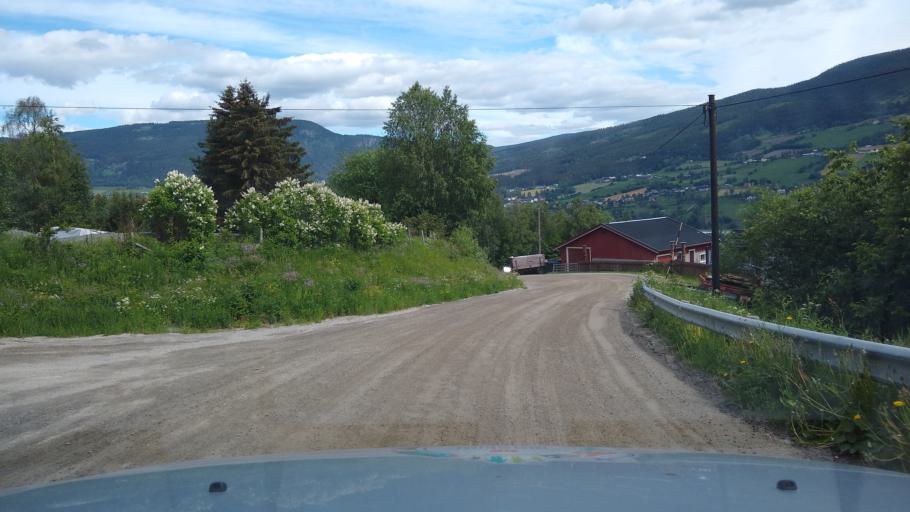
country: NO
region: Oppland
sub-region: Ringebu
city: Ringebu
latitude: 61.5169
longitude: 10.1322
